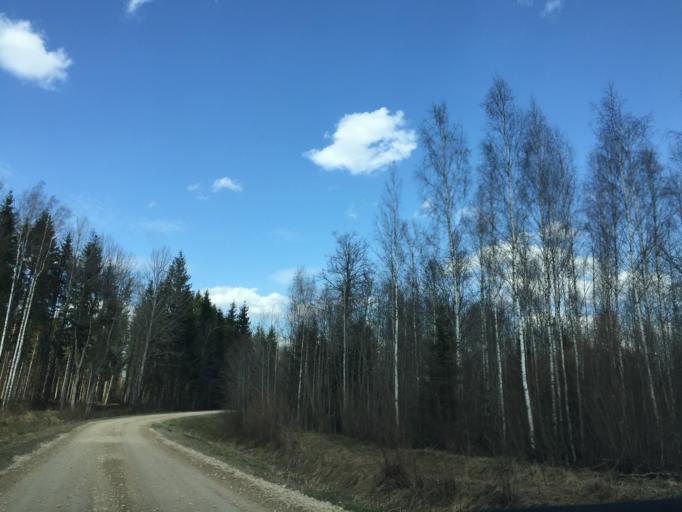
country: LV
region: Skriveri
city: Skriveri
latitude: 56.8001
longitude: 25.1736
